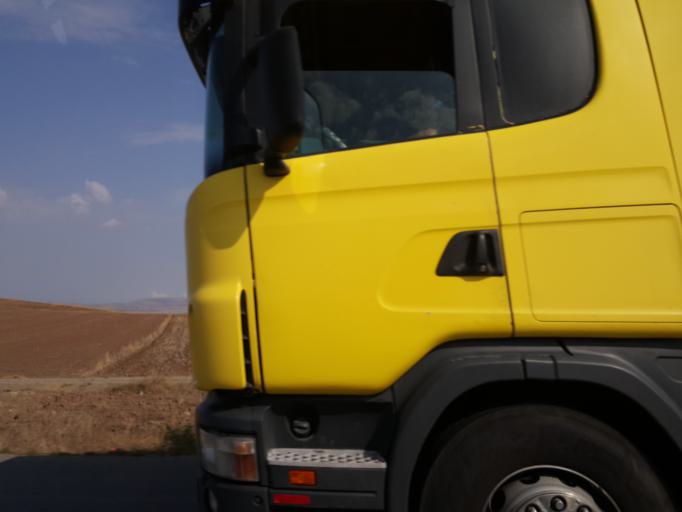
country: TR
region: Corum
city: Alaca
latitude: 40.1458
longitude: 34.8891
